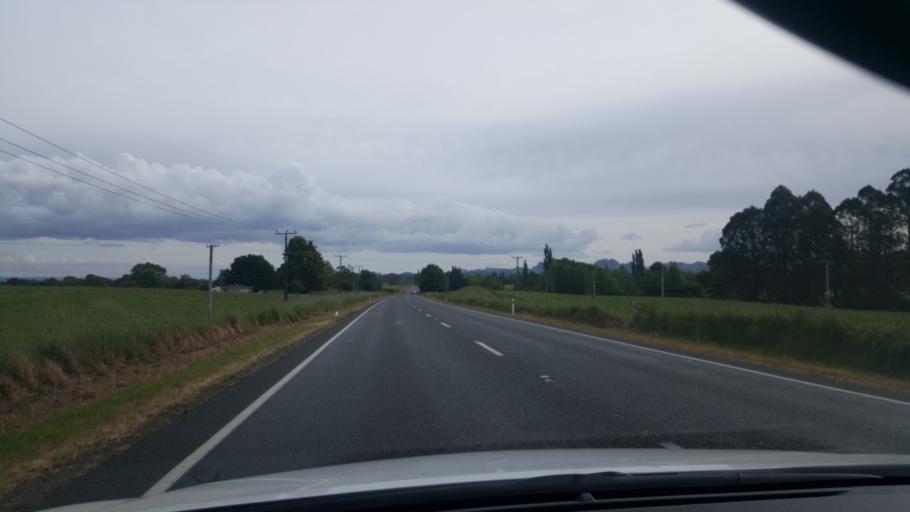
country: NZ
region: Bay of Plenty
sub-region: Rotorua District
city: Rotorua
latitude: -38.3969
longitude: 176.3350
